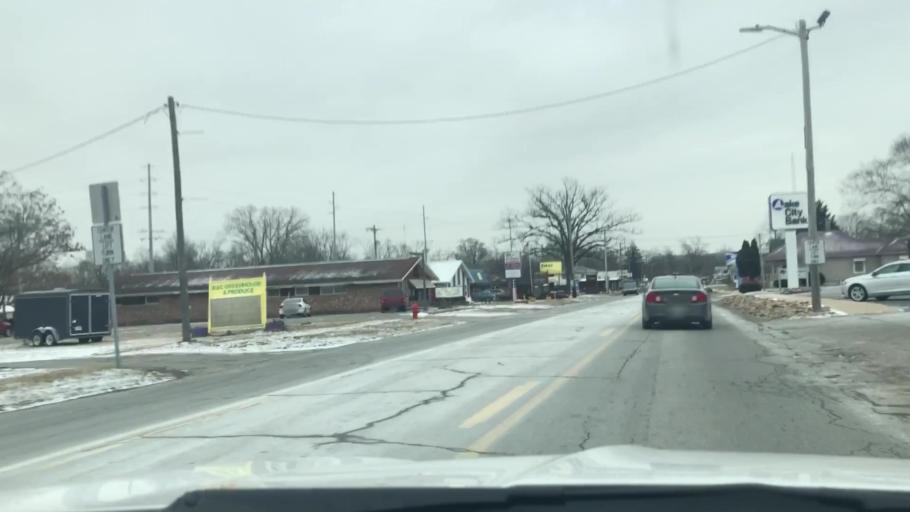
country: US
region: Indiana
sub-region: Fulton County
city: Rochester
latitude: 41.0646
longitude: -86.2108
